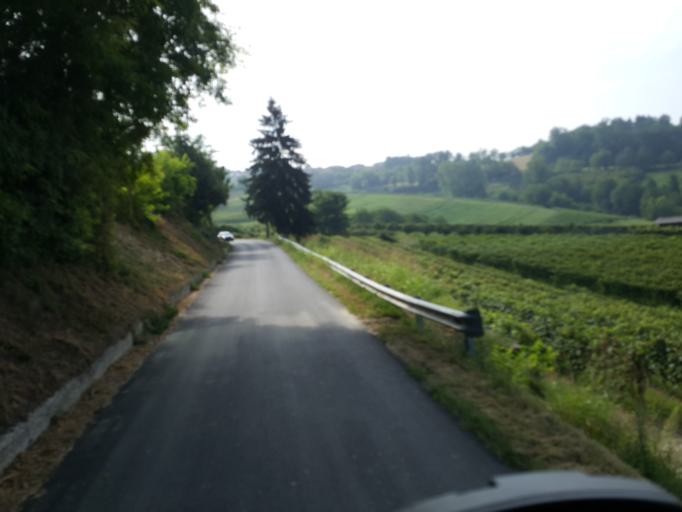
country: IT
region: Piedmont
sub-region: Provincia di Cuneo
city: Novello
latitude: 44.5914
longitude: 7.9184
